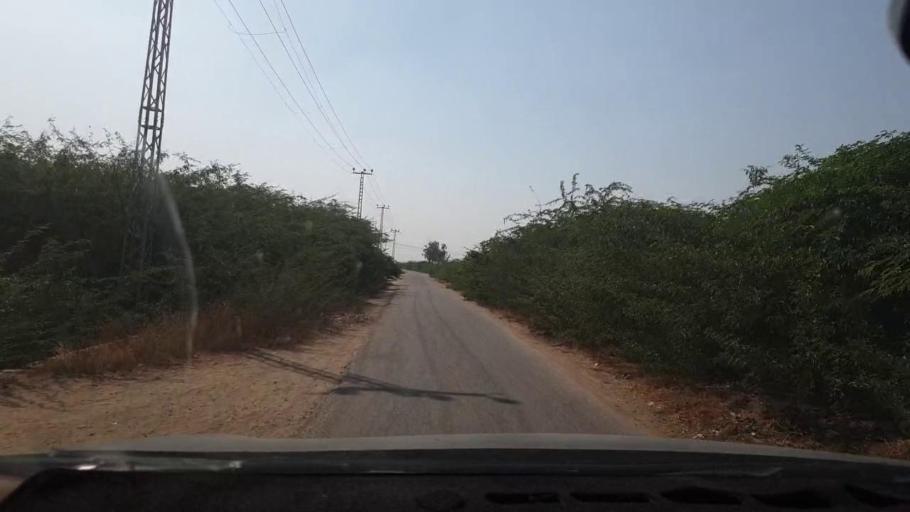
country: PK
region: Sindh
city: Malir Cantonment
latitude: 25.1139
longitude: 67.2084
